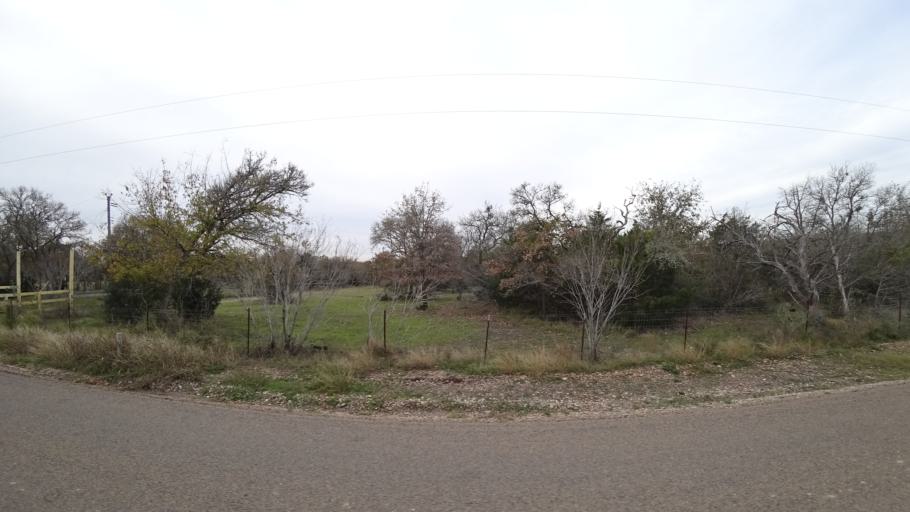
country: US
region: Texas
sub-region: Travis County
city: Garfield
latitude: 30.1085
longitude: -97.5614
